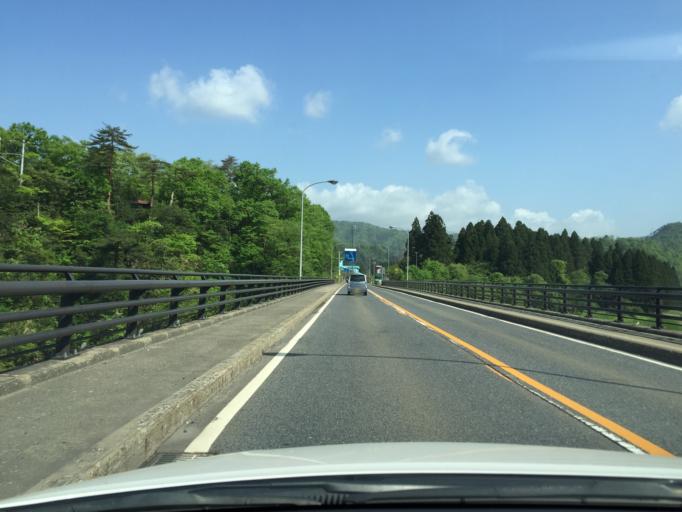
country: JP
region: Niigata
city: Suibara
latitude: 37.7147
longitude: 139.3804
